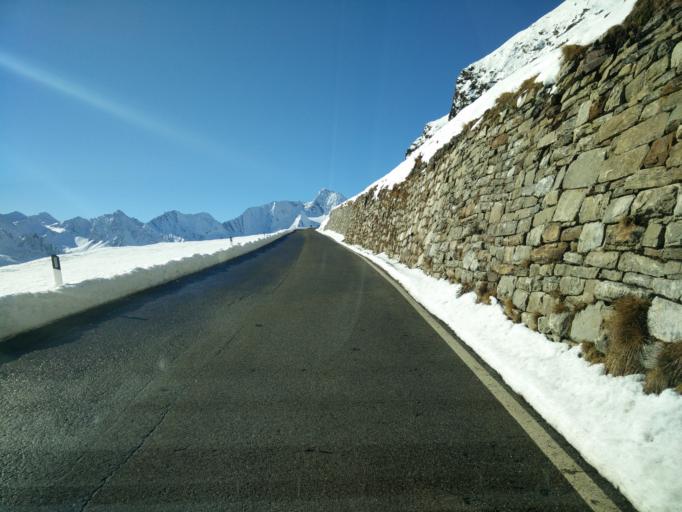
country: IT
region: Trentino-Alto Adige
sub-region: Bolzano
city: Moso in Passiria
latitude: 46.8879
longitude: 11.1125
